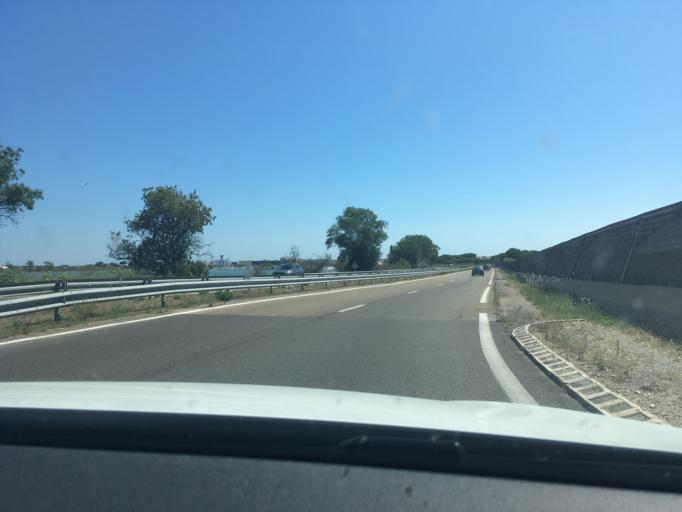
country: FR
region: Languedoc-Roussillon
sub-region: Departement du Gard
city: Le Grau-du-Roi
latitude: 43.5481
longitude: 4.1339
